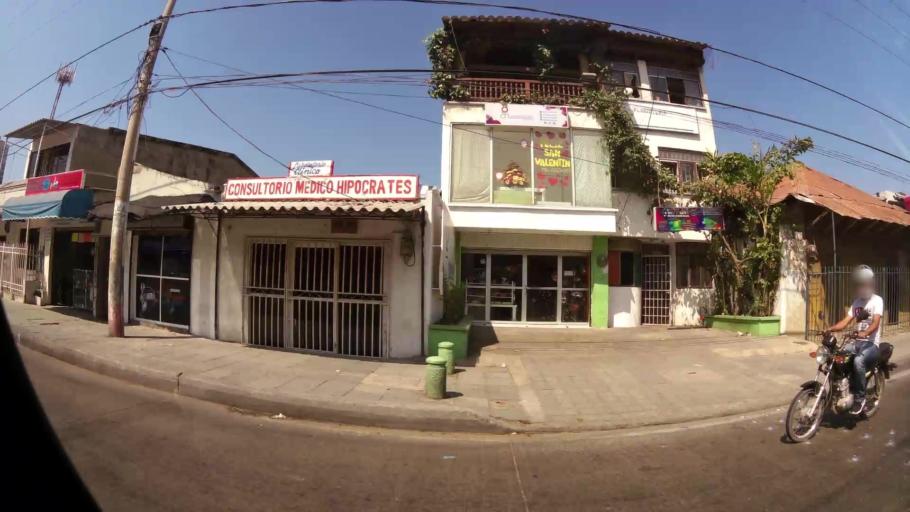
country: CO
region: Bolivar
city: Cartagena
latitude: 10.4076
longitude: -75.5080
